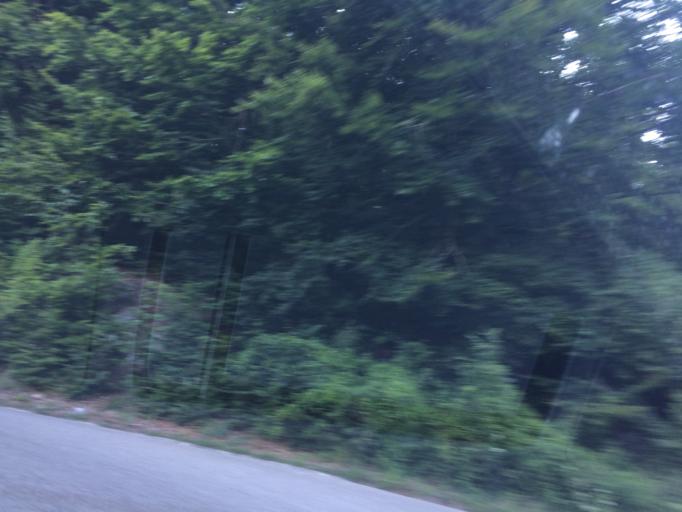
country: ME
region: Opstina Savnik
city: Savnik
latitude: 42.9489
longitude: 19.0917
